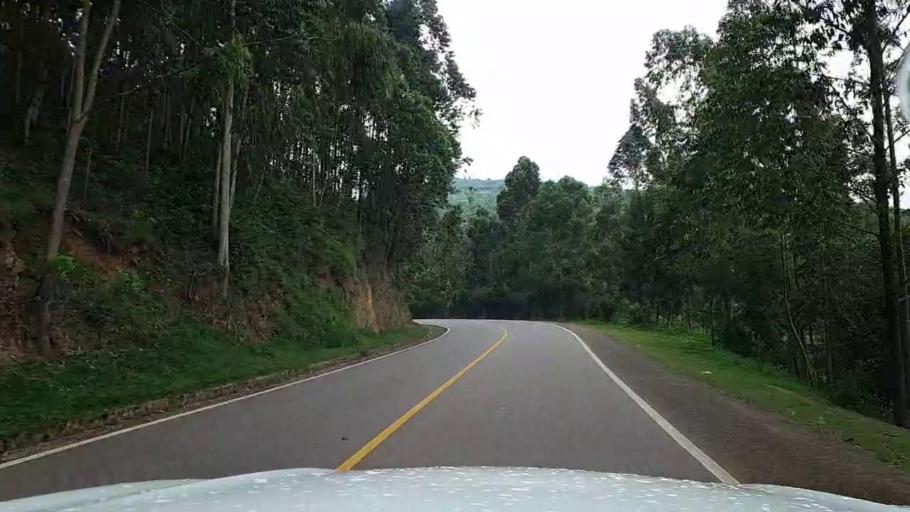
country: RW
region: Northern Province
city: Byumba
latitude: -1.7163
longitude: 30.1218
